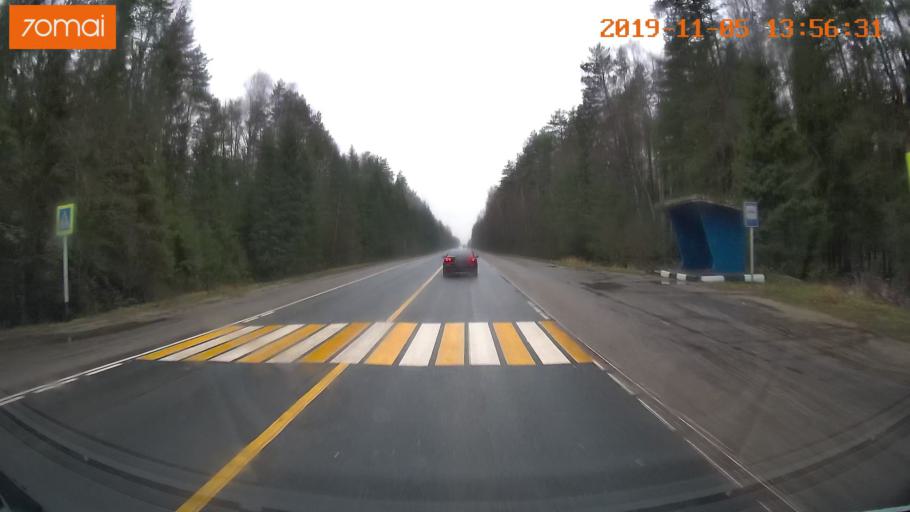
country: RU
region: Ivanovo
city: Kitovo
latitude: 57.0384
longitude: 41.3308
